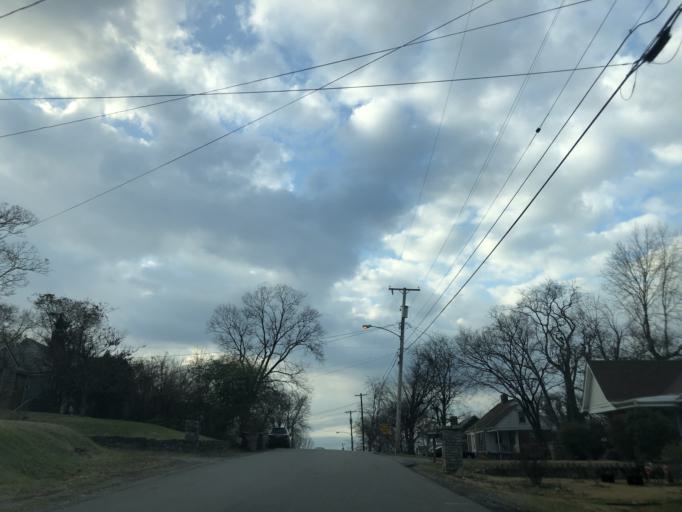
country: US
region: Tennessee
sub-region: Davidson County
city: Nashville
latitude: 36.2078
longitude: -86.7398
